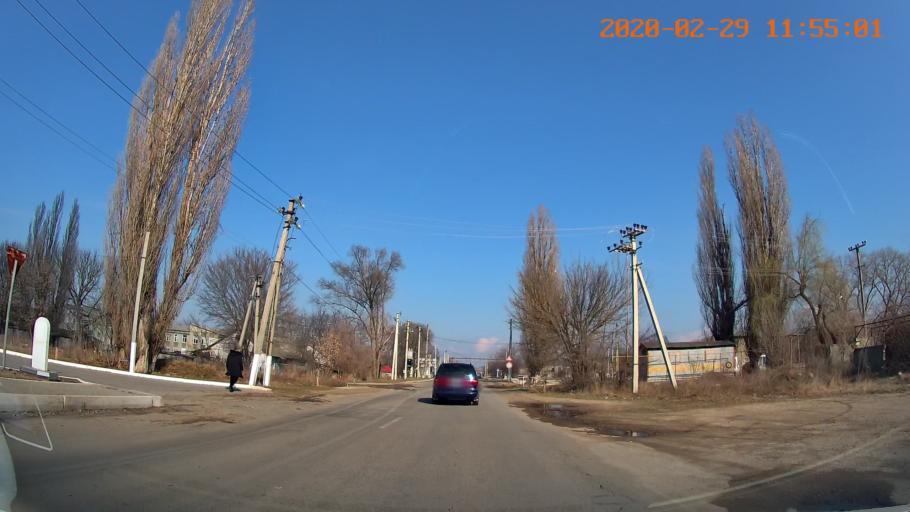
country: MD
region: Telenesti
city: Ribnita
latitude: 47.7876
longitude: 28.9968
